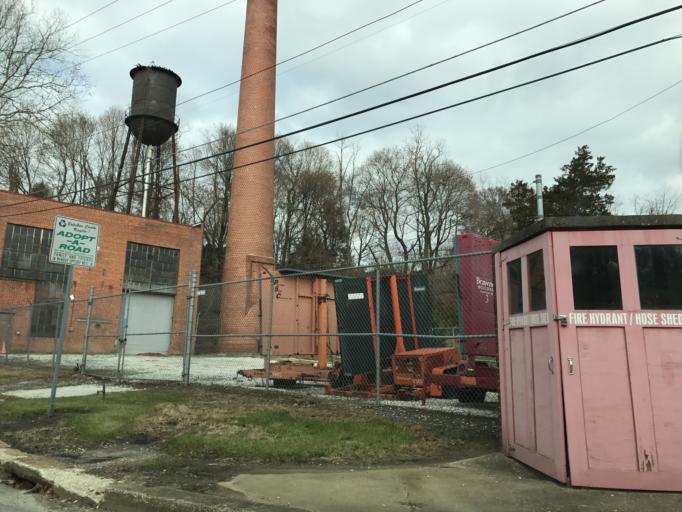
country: US
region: Maryland
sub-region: Baltimore County
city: Hunt Valley
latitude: 39.6185
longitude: -76.6280
